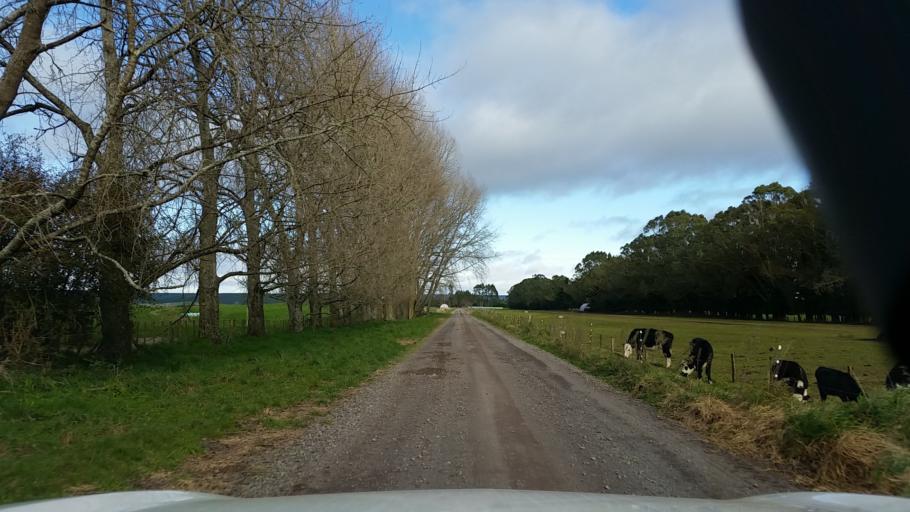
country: NZ
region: Bay of Plenty
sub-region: Whakatane District
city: Murupara
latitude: -38.4708
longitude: 176.4169
